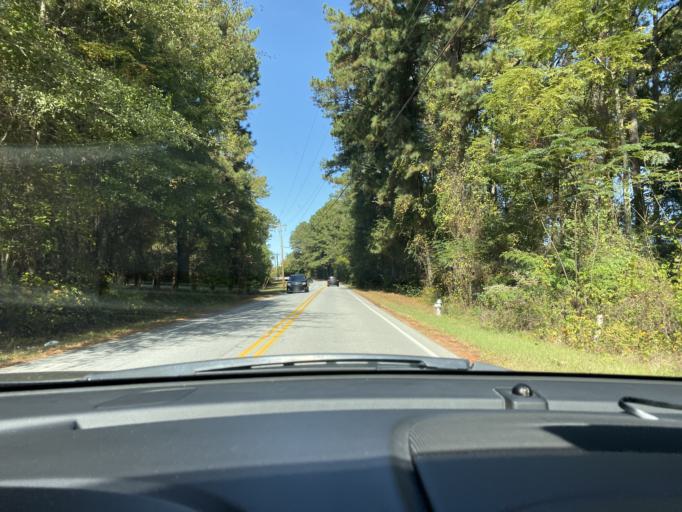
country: US
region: Georgia
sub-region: Walton County
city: Loganville
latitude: 33.8692
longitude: -83.9098
